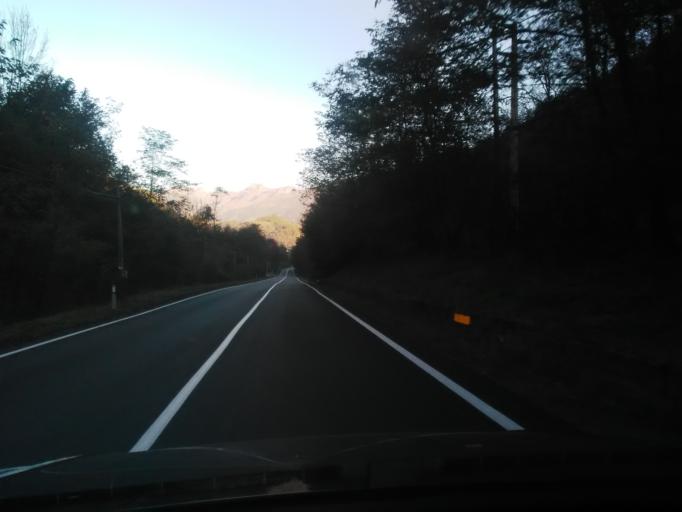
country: IT
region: Piedmont
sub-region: Provincia di Biella
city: Crevacuore
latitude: 45.6749
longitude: 8.2540
